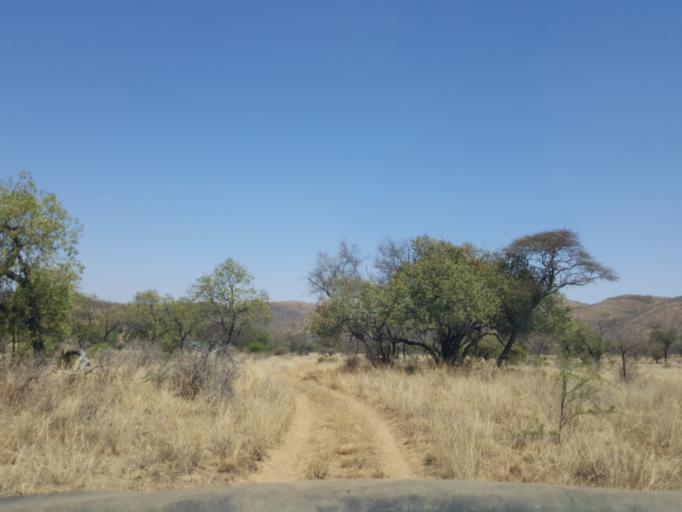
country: BW
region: South East
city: Lobatse
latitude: -25.1369
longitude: 25.6720
